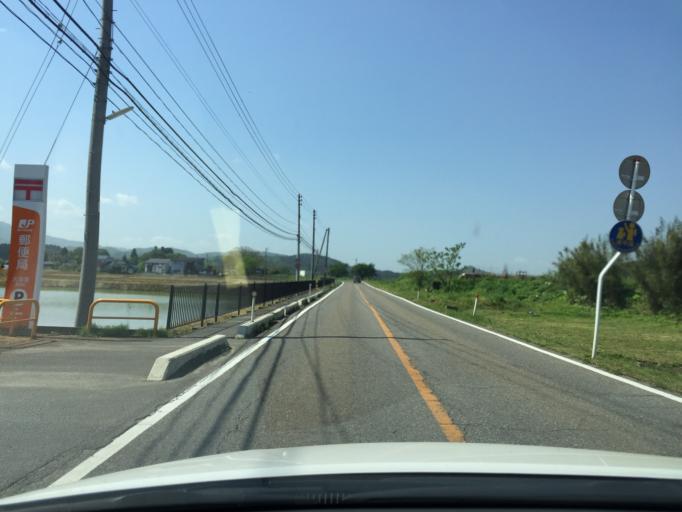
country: JP
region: Niigata
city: Muramatsu
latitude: 37.6818
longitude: 139.1503
